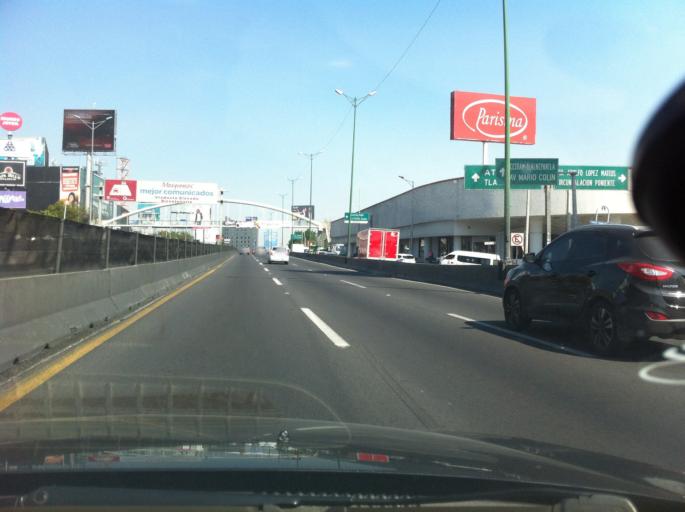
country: MX
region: Mexico
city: Vista Hermosa
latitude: 19.5055
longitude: -99.2367
